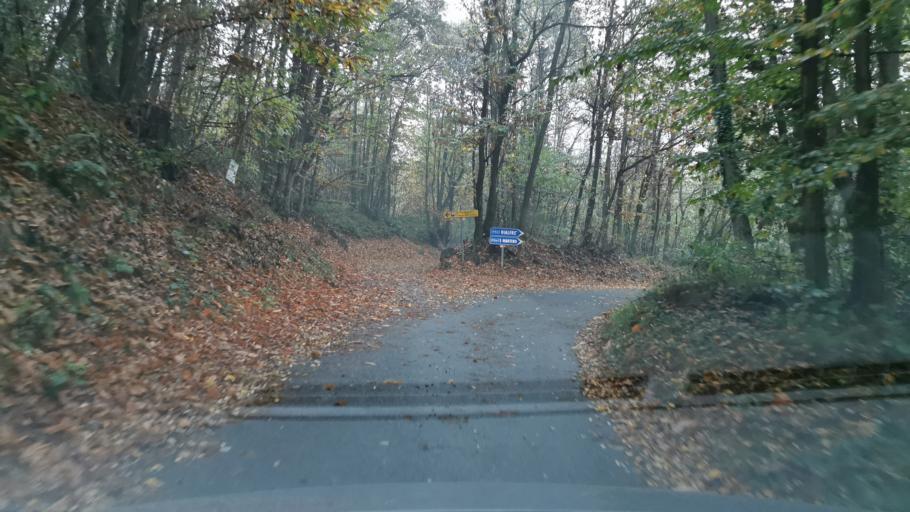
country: IT
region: Piedmont
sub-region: Provincia di Torino
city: Vialfre
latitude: 45.3723
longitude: 7.8016
